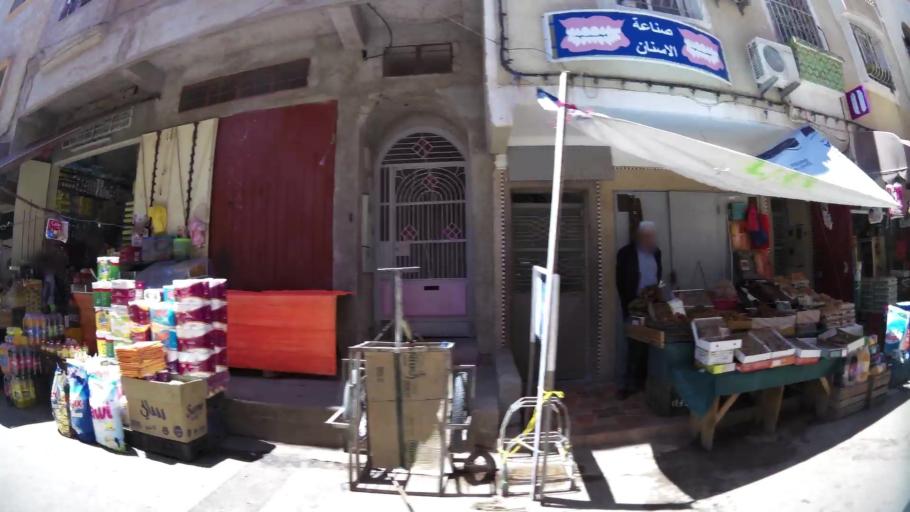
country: MA
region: Oriental
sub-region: Oujda-Angad
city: Oujda
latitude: 34.6607
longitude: -1.9228
